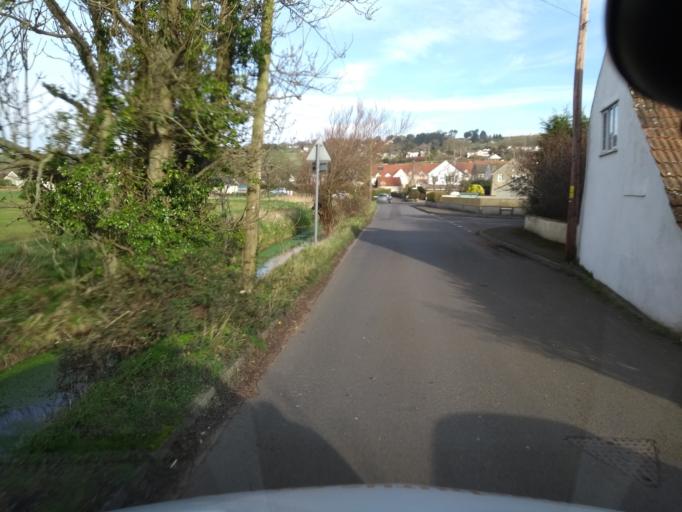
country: GB
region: England
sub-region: North Somerset
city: Bleadon
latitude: 51.3060
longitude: -2.9485
